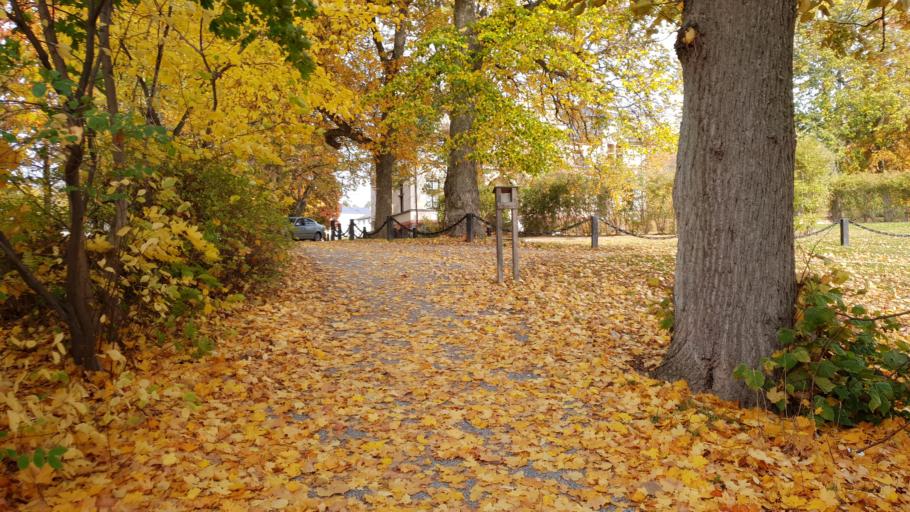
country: SE
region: Stockholm
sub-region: Stockholms Kommun
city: Bromma
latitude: 59.3401
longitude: 17.8770
